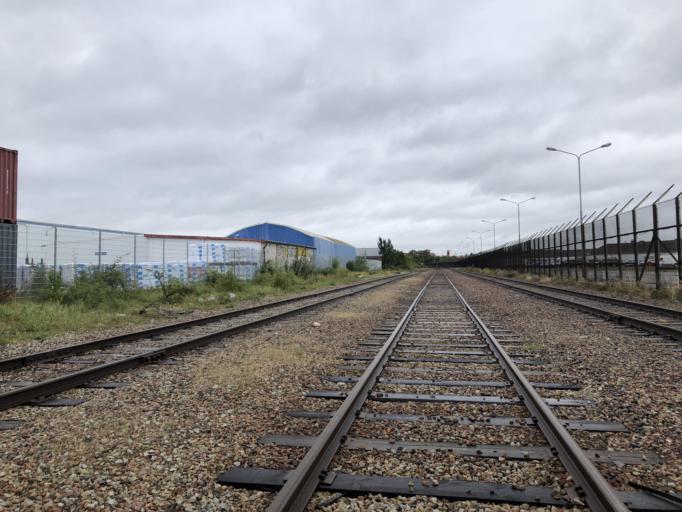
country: SE
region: Skane
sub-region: Malmo
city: Malmoe
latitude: 55.6180
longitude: 13.0173
